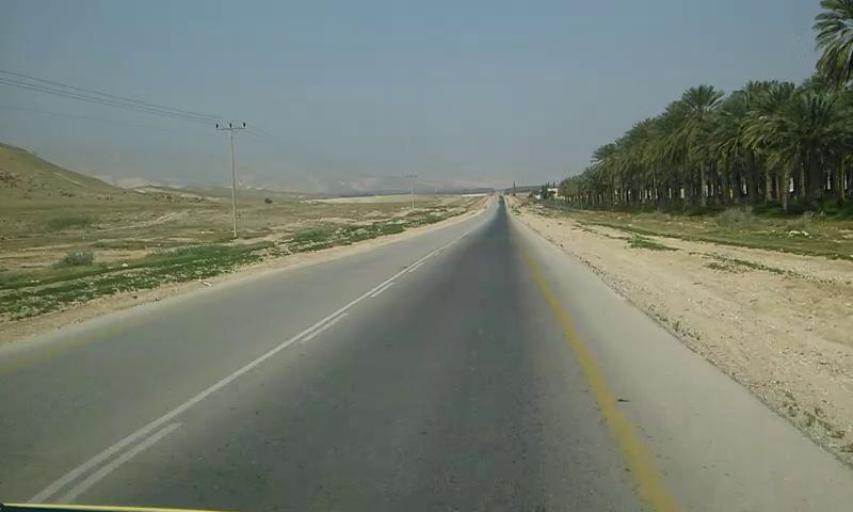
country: PS
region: West Bank
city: Al `Awja
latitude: 31.9800
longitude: 35.4661
